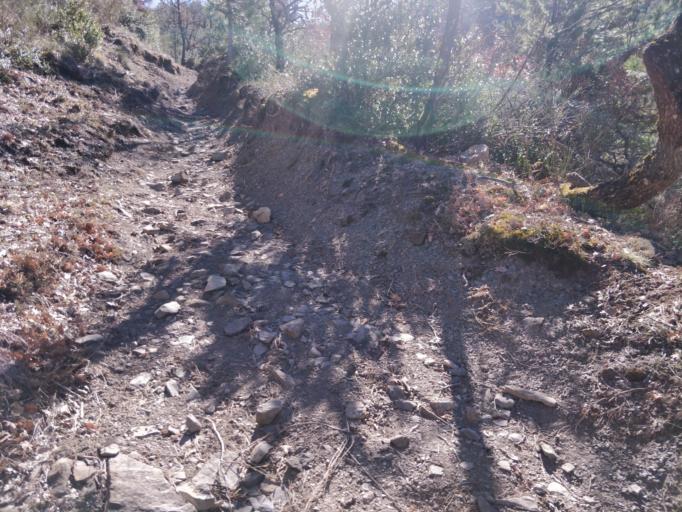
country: FR
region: Provence-Alpes-Cote d'Azur
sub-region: Departement des Alpes-de-Haute-Provence
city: Digne-les-Bains
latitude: 44.0986
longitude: 6.2529
